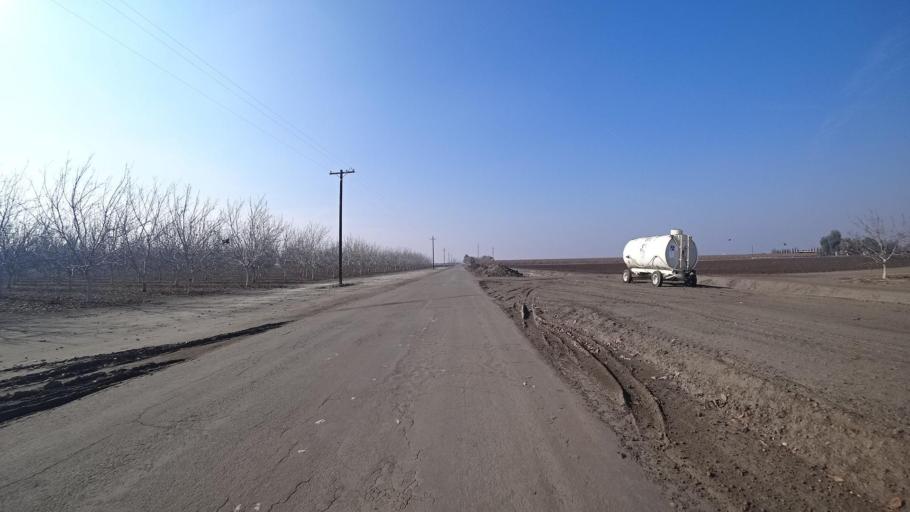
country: US
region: California
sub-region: Kern County
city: Buttonwillow
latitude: 35.3693
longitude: -119.4230
